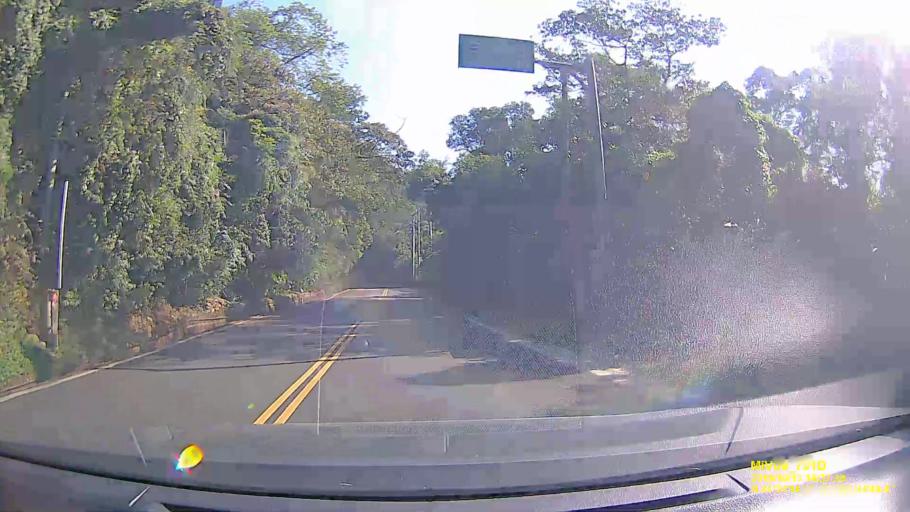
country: TW
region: Taiwan
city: Fengyuan
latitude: 24.4038
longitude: 120.7471
